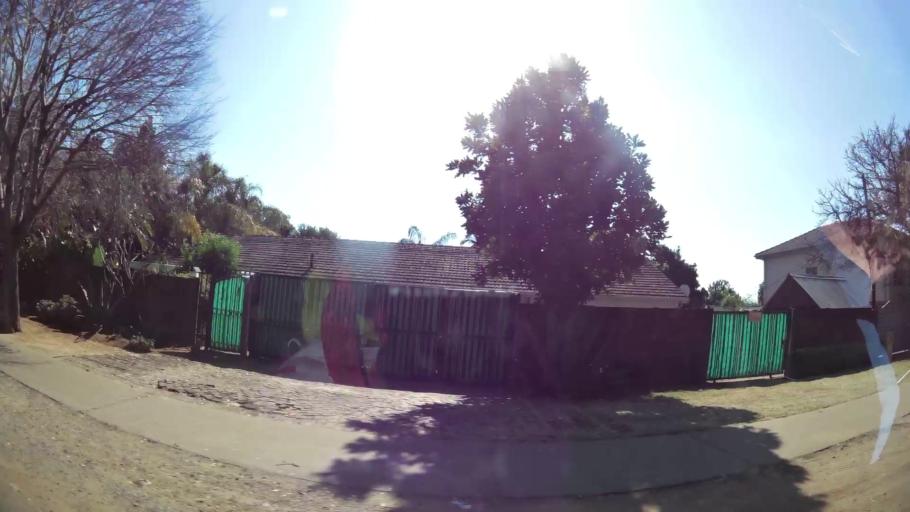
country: ZA
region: Gauteng
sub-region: City of Tshwane Metropolitan Municipality
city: Pretoria
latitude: -25.6866
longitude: 28.2256
